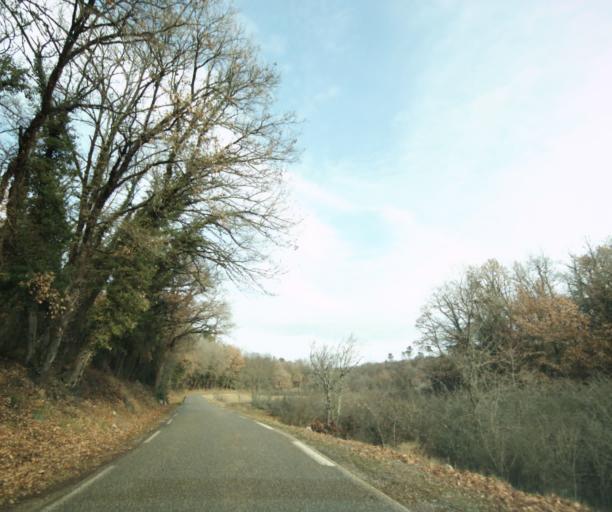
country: FR
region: Provence-Alpes-Cote d'Azur
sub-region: Departement du Var
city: Rougiers
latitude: 43.4133
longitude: 5.8688
